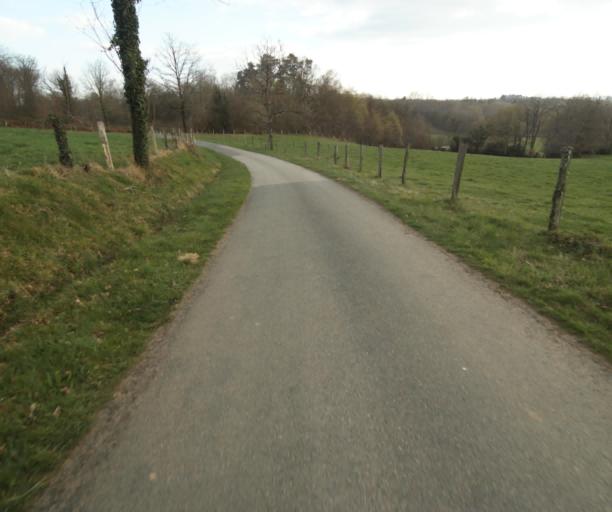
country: FR
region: Limousin
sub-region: Departement de la Correze
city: Saint-Clement
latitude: 45.3649
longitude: 1.6367
